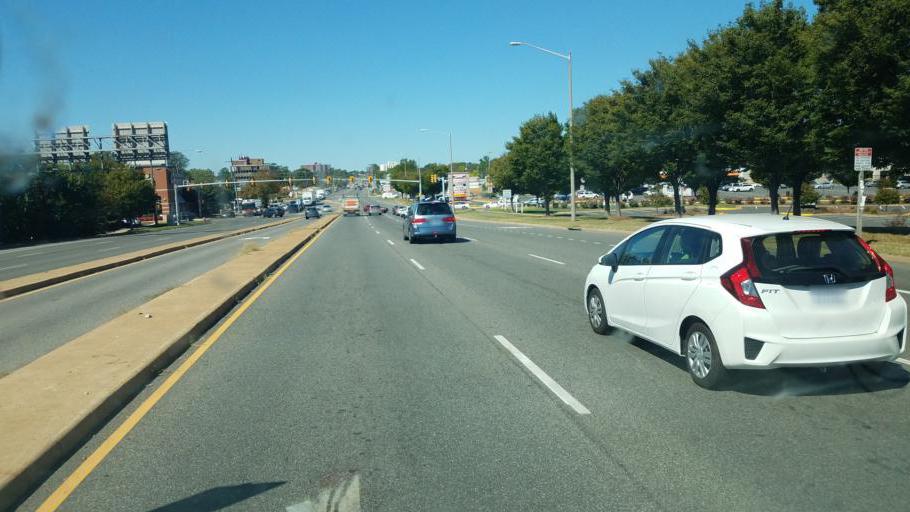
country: US
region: Virginia
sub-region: Fairfax County
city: Baileys Crossroads
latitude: 38.8511
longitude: -77.1305
